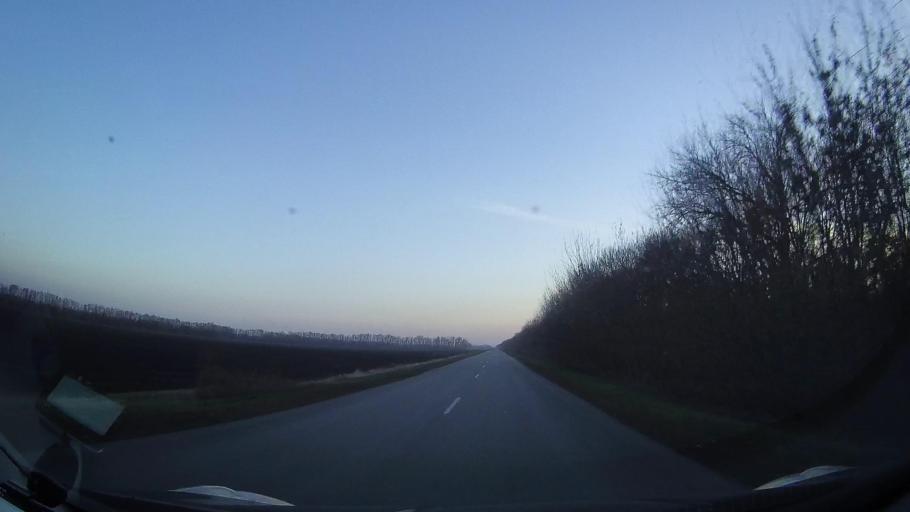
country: RU
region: Rostov
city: Zernograd
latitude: 47.0158
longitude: 40.3916
